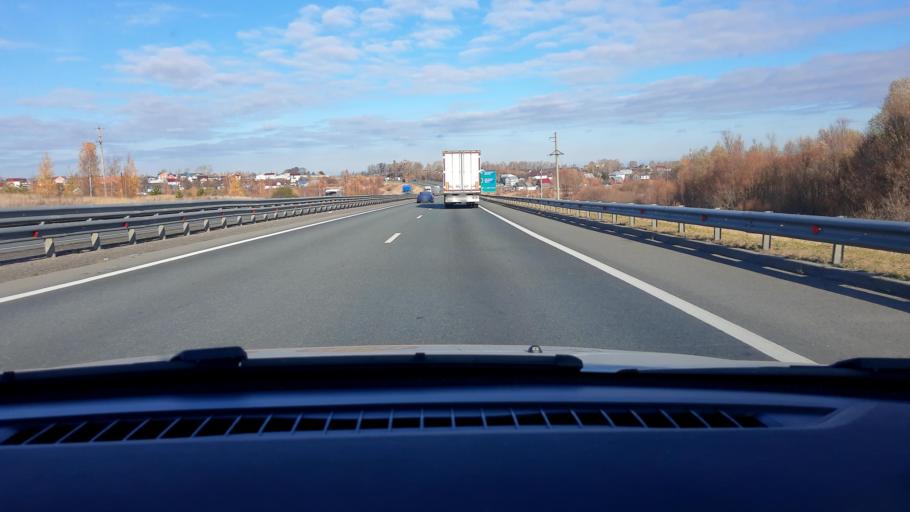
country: RU
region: Nizjnij Novgorod
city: Burevestnik
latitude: 56.1587
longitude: 43.7489
